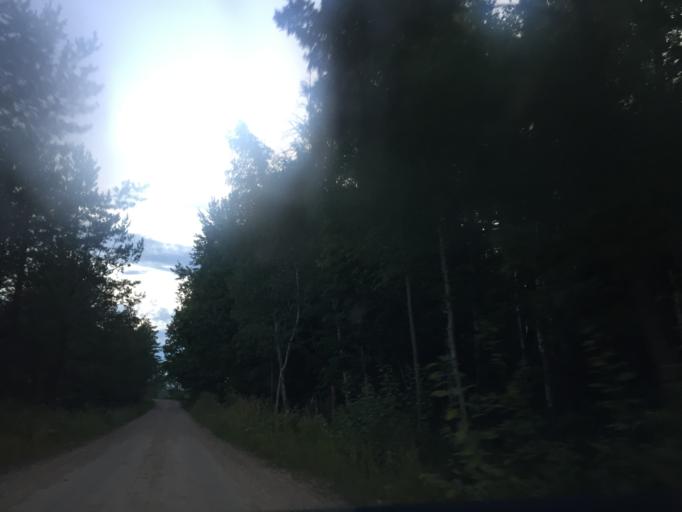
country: LV
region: Koknese
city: Koknese
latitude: 56.6213
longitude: 25.4886
